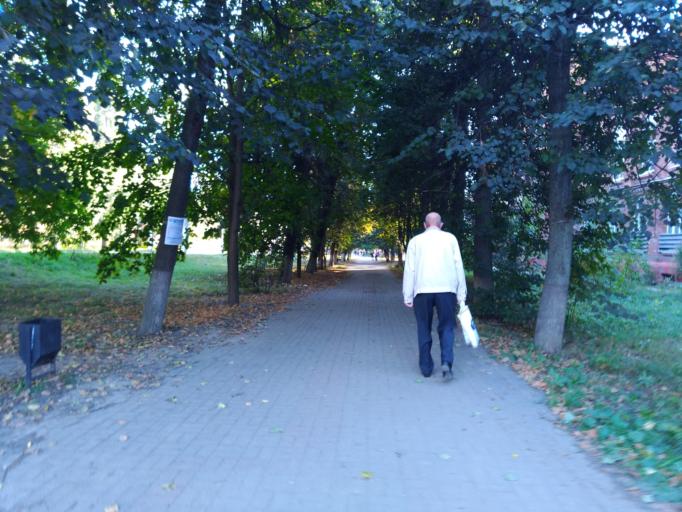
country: RU
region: Kaluga
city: Kaluga
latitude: 54.5301
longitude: 36.2747
